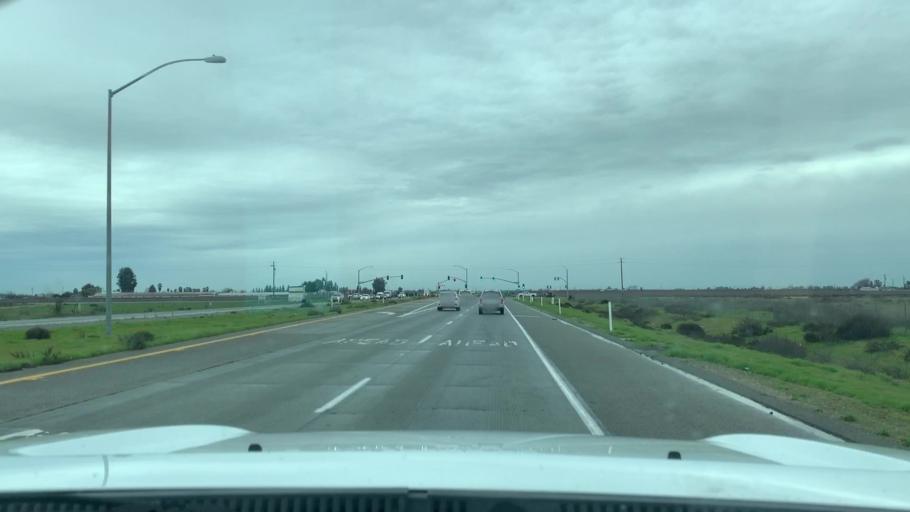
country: US
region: California
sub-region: Fresno County
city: Caruthers
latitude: 36.5451
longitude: -119.7860
